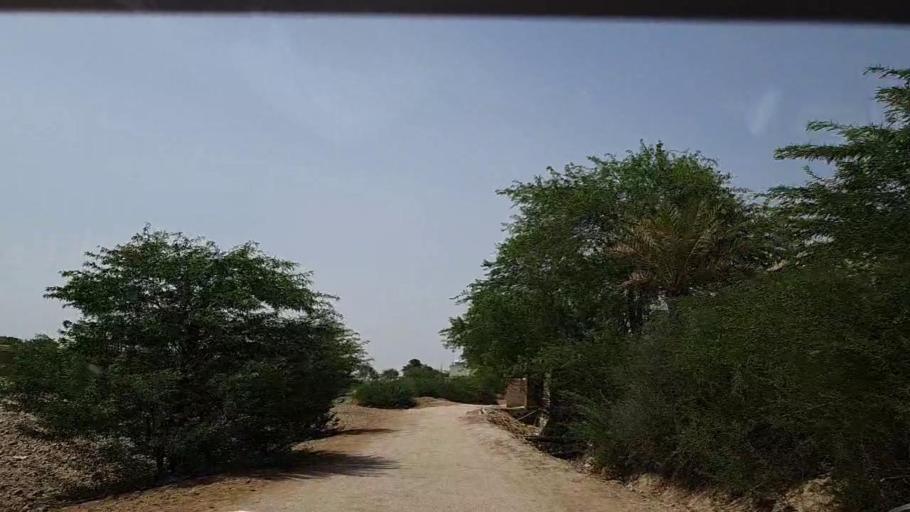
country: PK
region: Sindh
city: Johi
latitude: 26.7865
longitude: 67.6201
